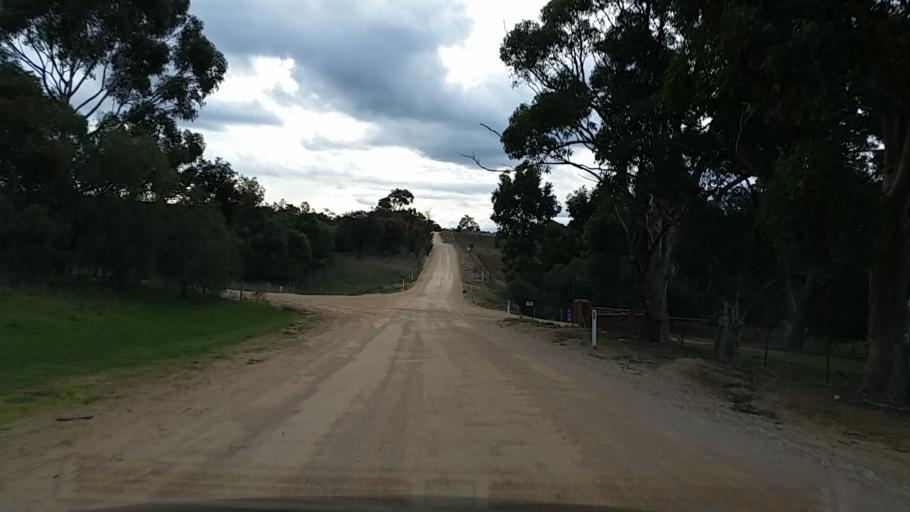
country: AU
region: South Australia
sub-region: Mount Barker
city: Nairne
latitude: -34.9797
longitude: 139.0348
